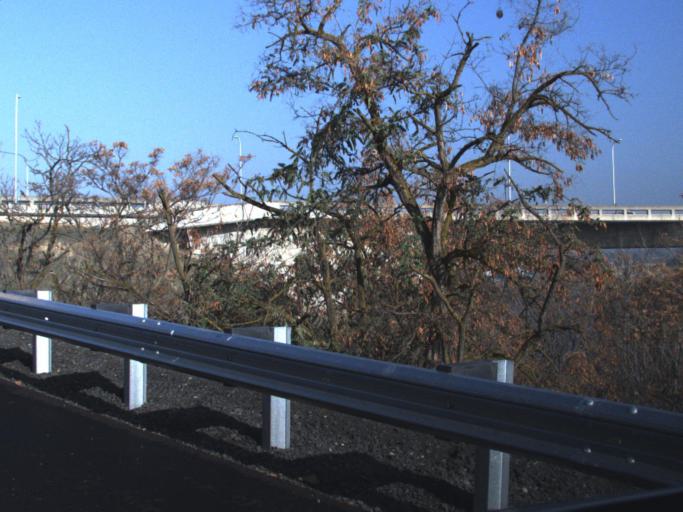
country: US
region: Washington
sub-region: Asotin County
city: Clarkston
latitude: 46.3960
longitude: -117.0443
